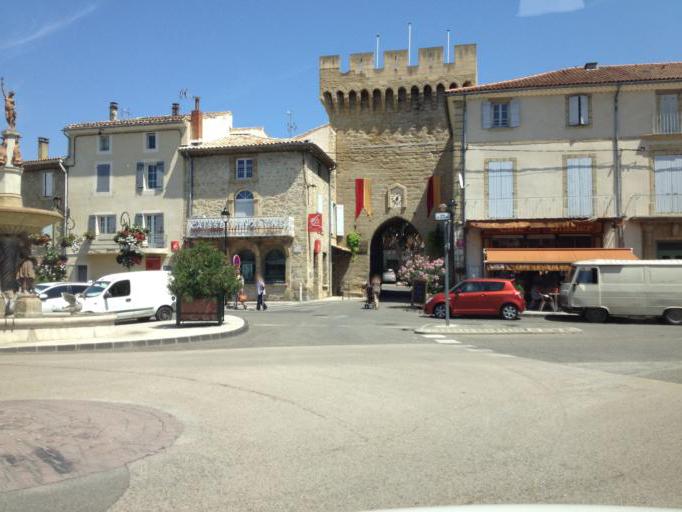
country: FR
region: Provence-Alpes-Cote d'Azur
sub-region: Departement du Vaucluse
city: Courthezon
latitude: 44.0854
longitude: 4.8822
